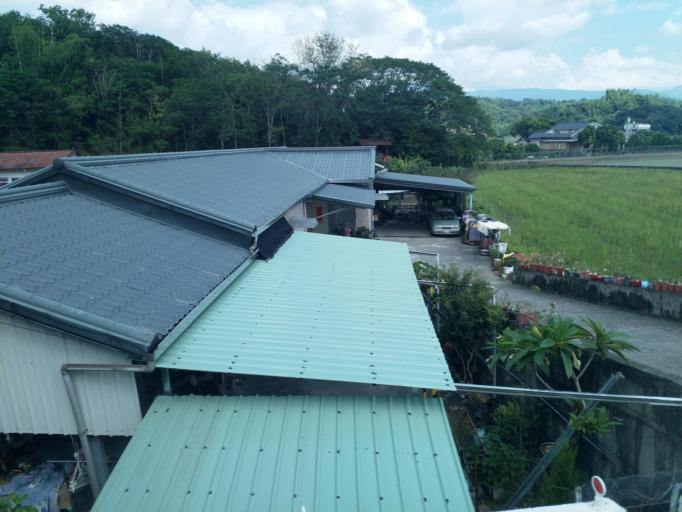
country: TW
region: Taiwan
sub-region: Pingtung
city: Pingtung
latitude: 22.8872
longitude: 120.5518
